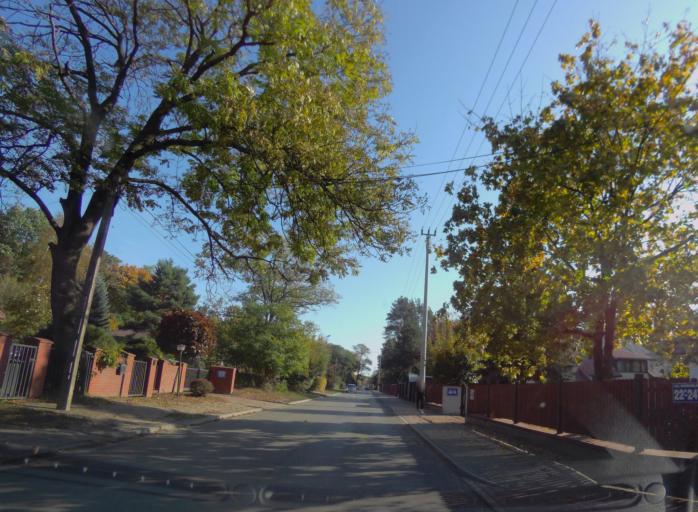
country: PL
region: Masovian Voivodeship
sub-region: Powiat otwocki
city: Jozefow
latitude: 52.1708
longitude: 21.2972
